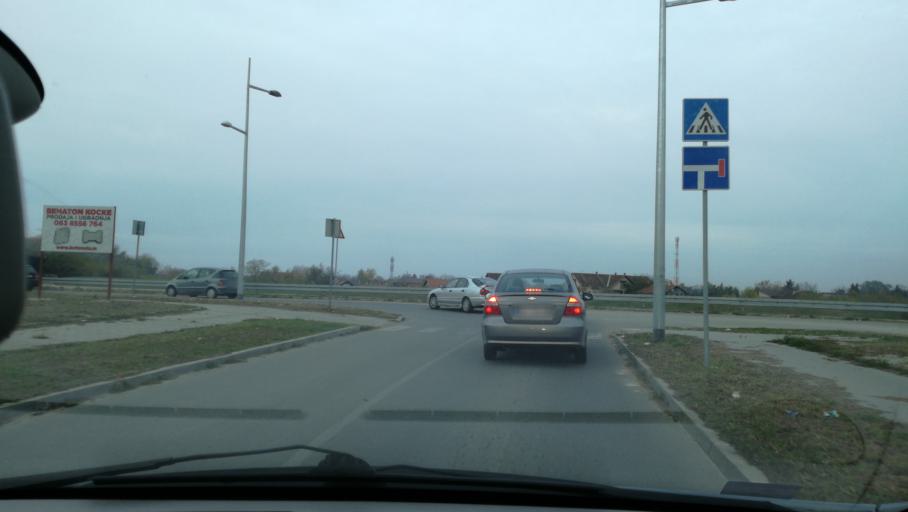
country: RS
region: Autonomna Pokrajina Vojvodina
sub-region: Juznobacki Okrug
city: Novi Sad
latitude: 45.2778
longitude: 19.8297
